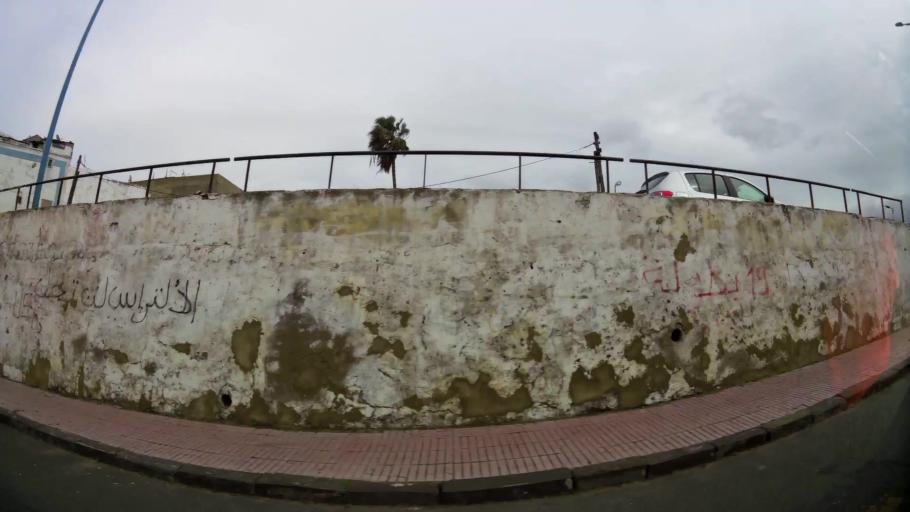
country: MA
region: Grand Casablanca
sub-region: Casablanca
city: Casablanca
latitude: 33.5710
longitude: -7.6078
